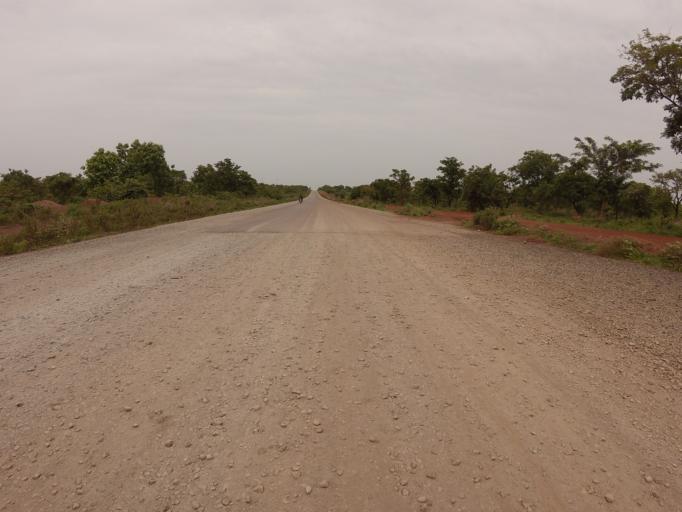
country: GH
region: Northern
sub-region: Yendi
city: Yendi
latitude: 9.1369
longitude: 0.0080
